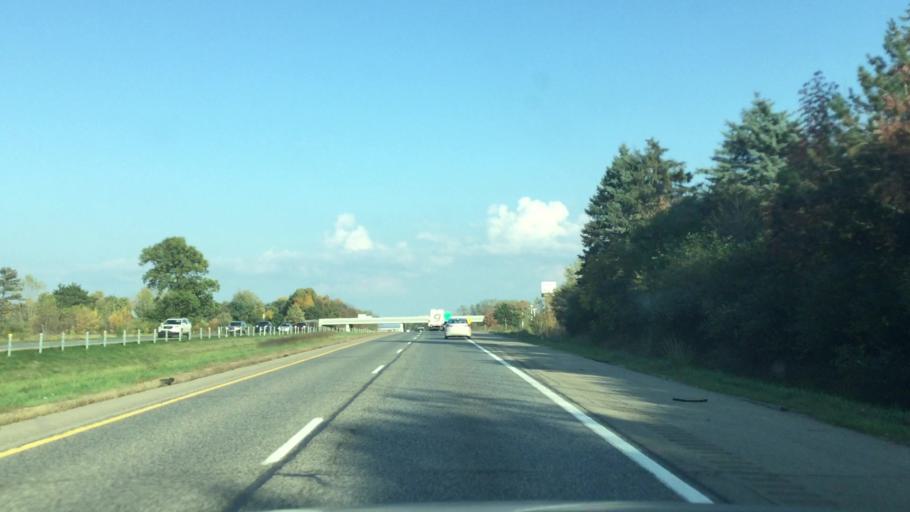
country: US
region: Michigan
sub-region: Washtenaw County
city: Chelsea
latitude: 42.2944
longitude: -84.0315
